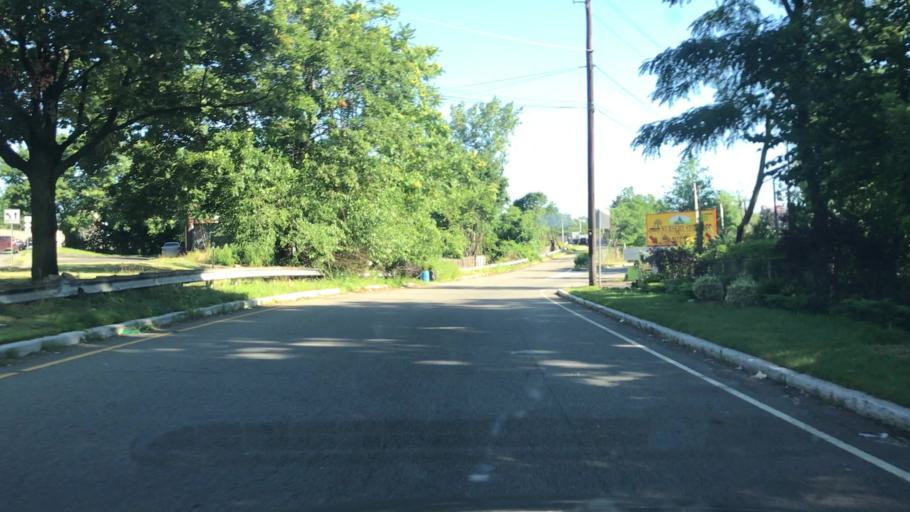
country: US
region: New Jersey
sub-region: Bergen County
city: Wallington
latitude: 40.8554
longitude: -74.1208
